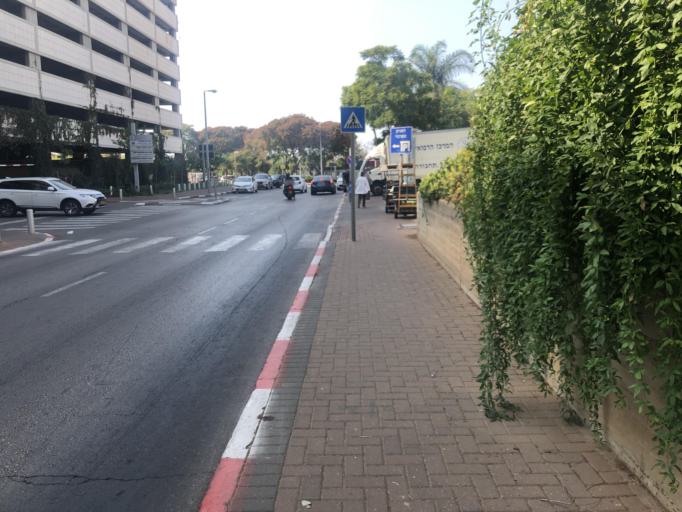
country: IL
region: Tel Aviv
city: Or Yehuda
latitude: 32.0480
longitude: 34.8425
